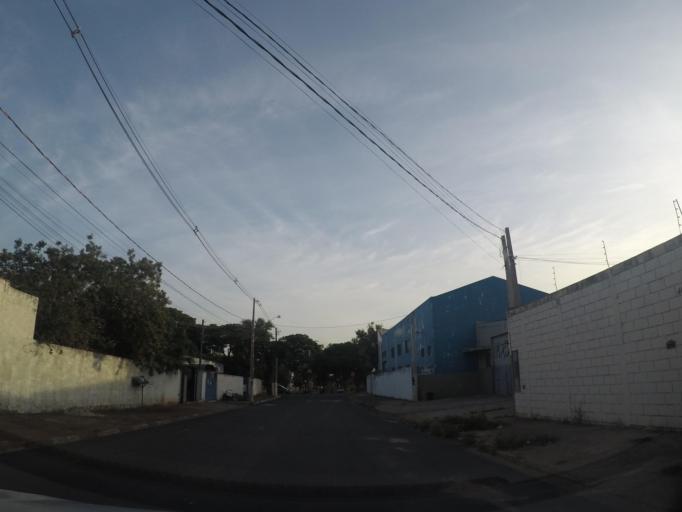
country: BR
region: Sao Paulo
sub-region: Hortolandia
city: Hortolandia
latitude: -22.8510
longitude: -47.1653
